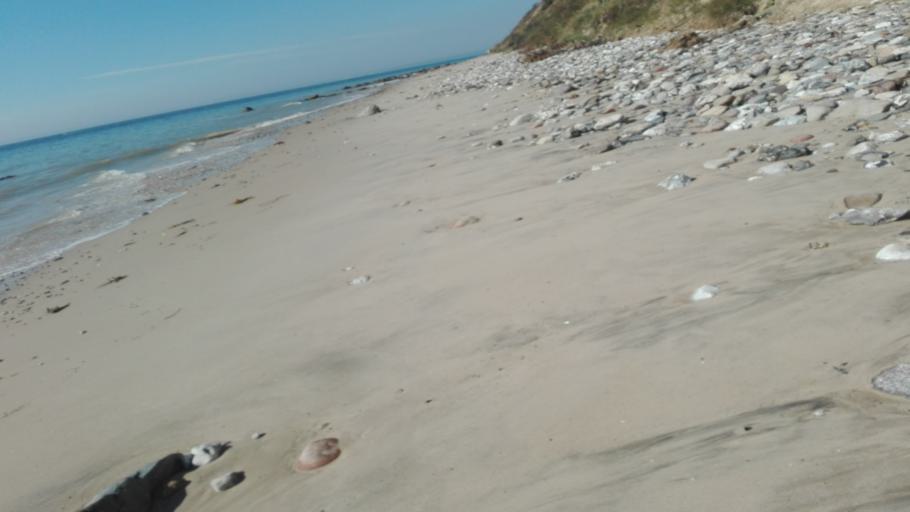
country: DK
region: Central Jutland
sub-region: Arhus Kommune
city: Logten
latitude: 56.1621
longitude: 10.3965
